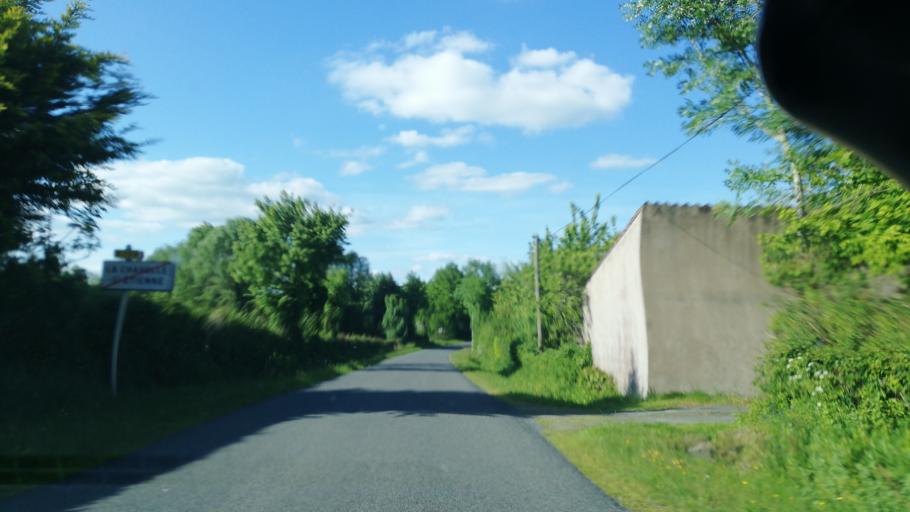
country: FR
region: Poitou-Charentes
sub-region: Departement des Deux-Sevres
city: Moncoutant
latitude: 46.6855
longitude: -0.5738
